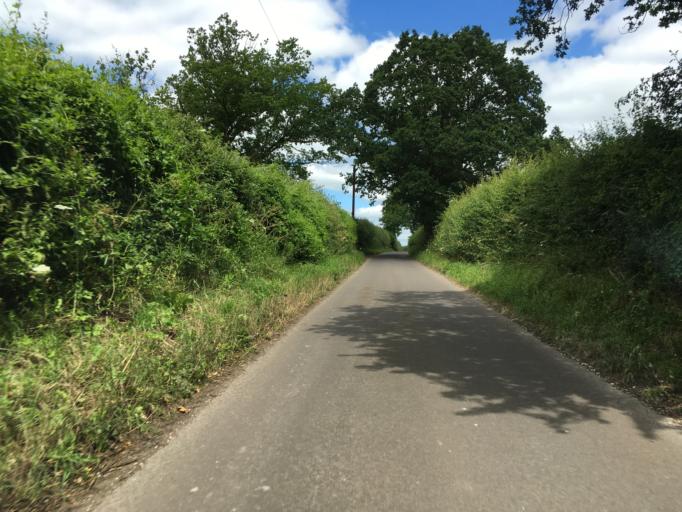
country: GB
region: England
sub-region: Hampshire
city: Highclere
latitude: 51.2687
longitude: -1.4173
